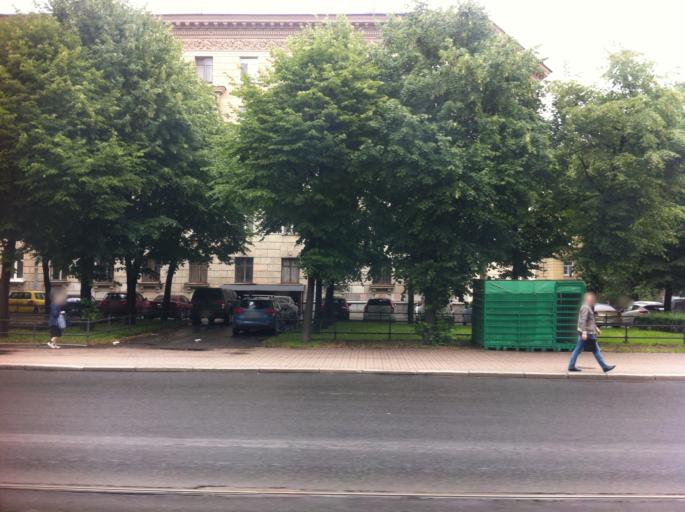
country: RU
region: St.-Petersburg
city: Admiralteisky
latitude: 59.9120
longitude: 30.2769
